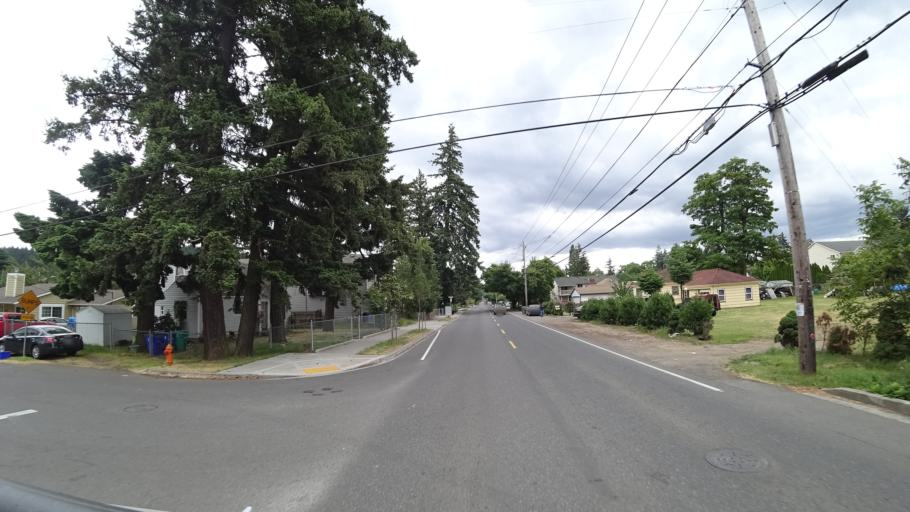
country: US
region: Oregon
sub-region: Multnomah County
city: Lents
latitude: 45.4952
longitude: -122.5235
